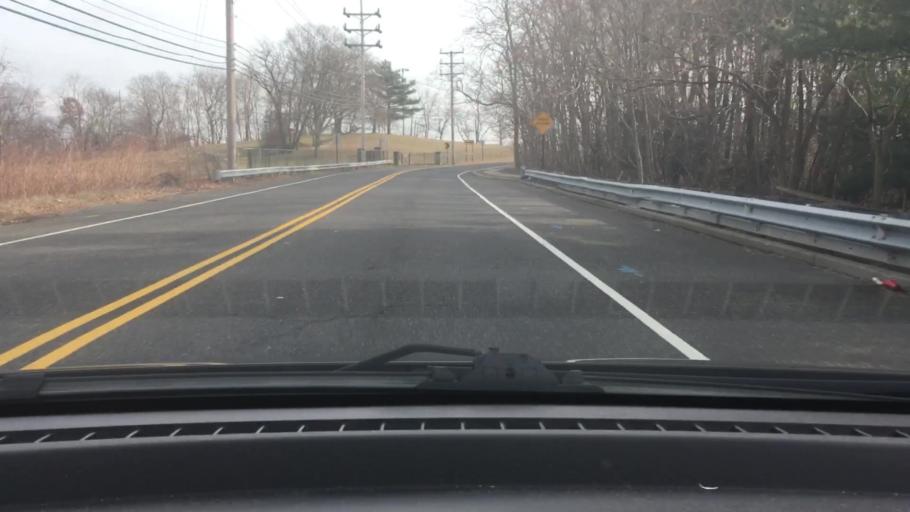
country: US
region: New Jersey
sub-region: Monmouth County
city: Shark River Hills
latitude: 40.2196
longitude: -74.0501
